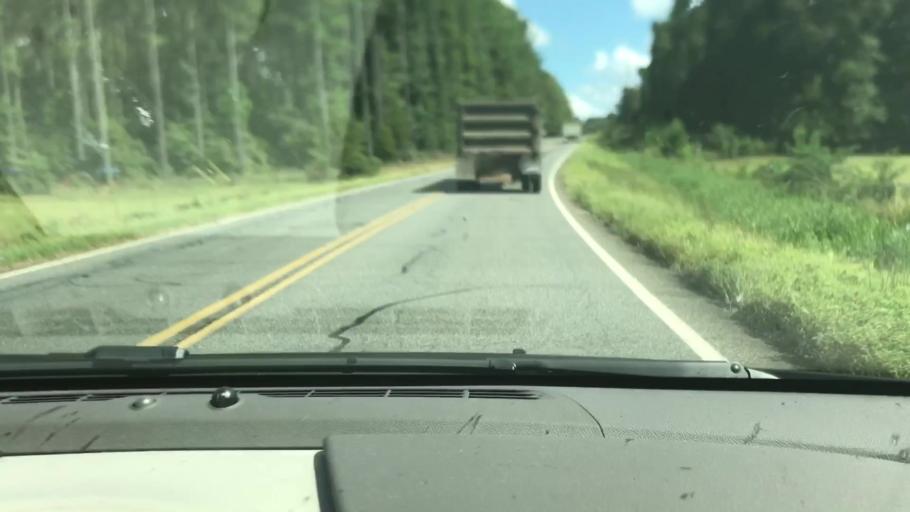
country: US
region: Alabama
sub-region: Chambers County
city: Valley
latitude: 32.8366
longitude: -85.0361
